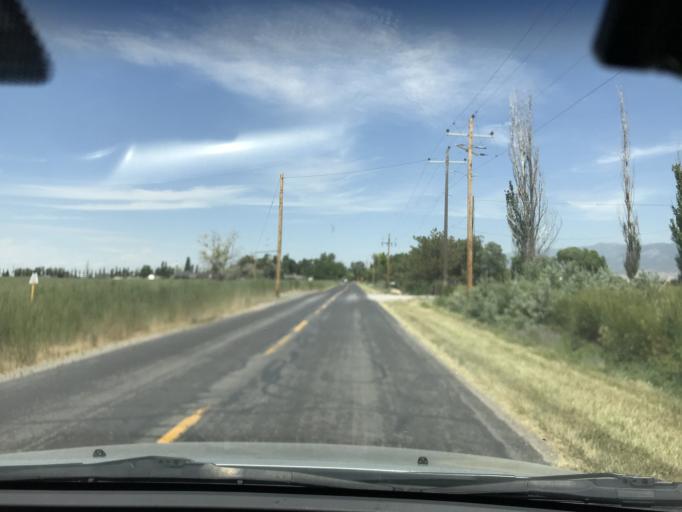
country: US
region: Utah
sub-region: Davis County
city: North Salt Lake
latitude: 40.8316
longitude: -111.9535
